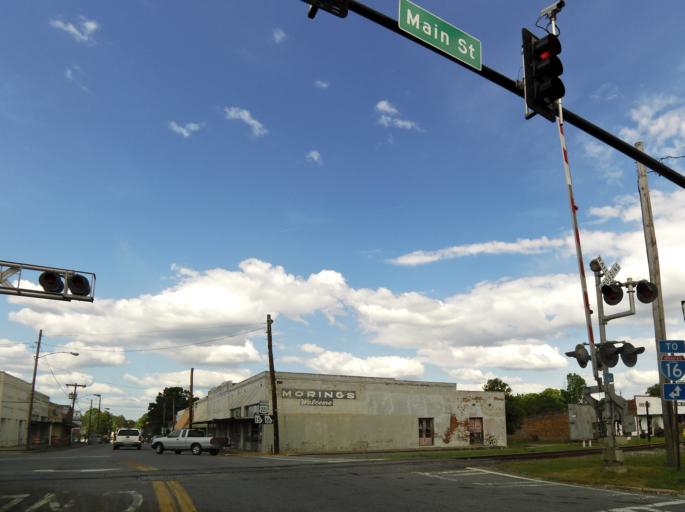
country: US
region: Georgia
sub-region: Treutlen County
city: Soperton
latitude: 32.3777
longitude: -82.5922
